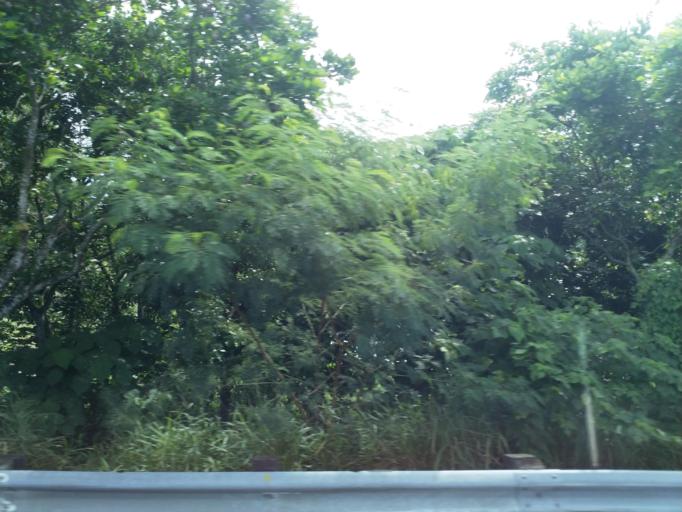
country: TW
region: Taiwan
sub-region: Pingtung
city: Pingtung
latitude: 22.8631
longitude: 120.4914
